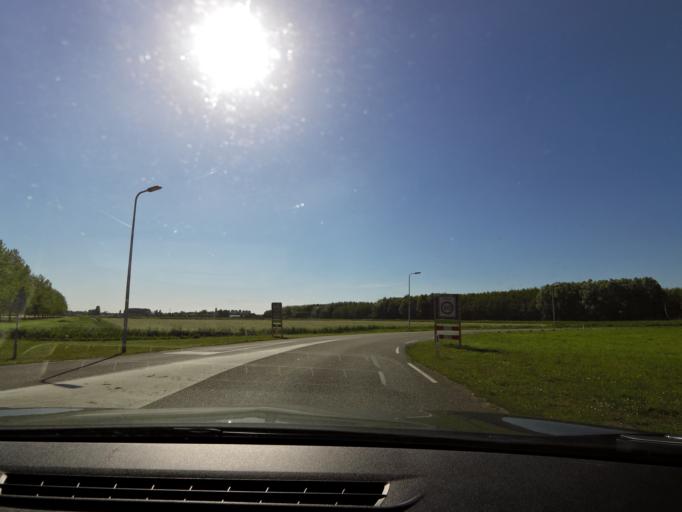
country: NL
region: South Holland
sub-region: Gemeente Hellevoetsluis
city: Nieuwenhoorn
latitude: 51.8535
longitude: 4.1617
